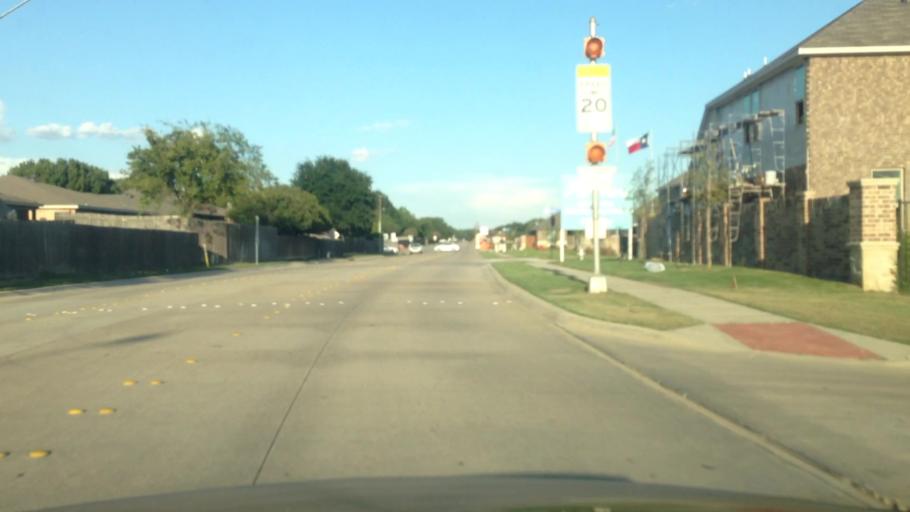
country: US
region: Texas
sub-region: Tarrant County
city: Watauga
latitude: 32.8822
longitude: -97.2569
